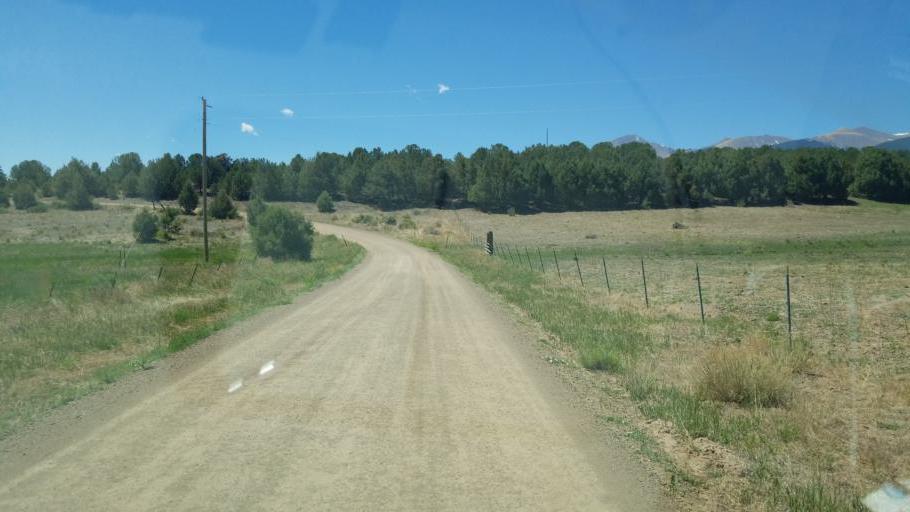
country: US
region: Colorado
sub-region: Custer County
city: Westcliffe
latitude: 38.2996
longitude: -105.6156
